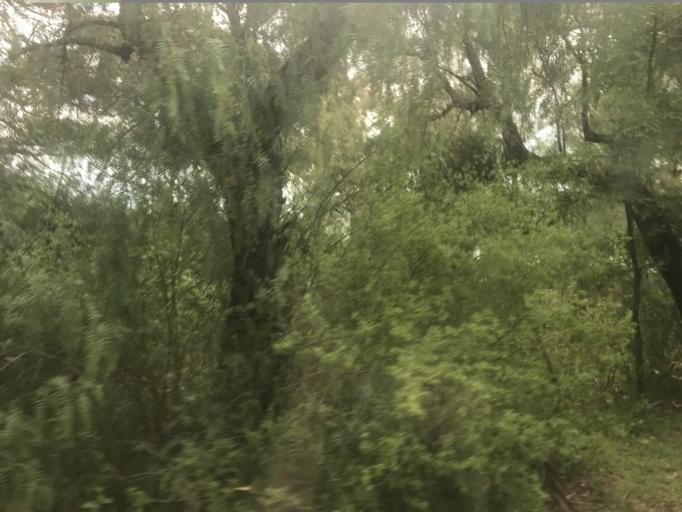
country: LS
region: Maseru
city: Nako
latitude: -29.6282
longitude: 27.5088
